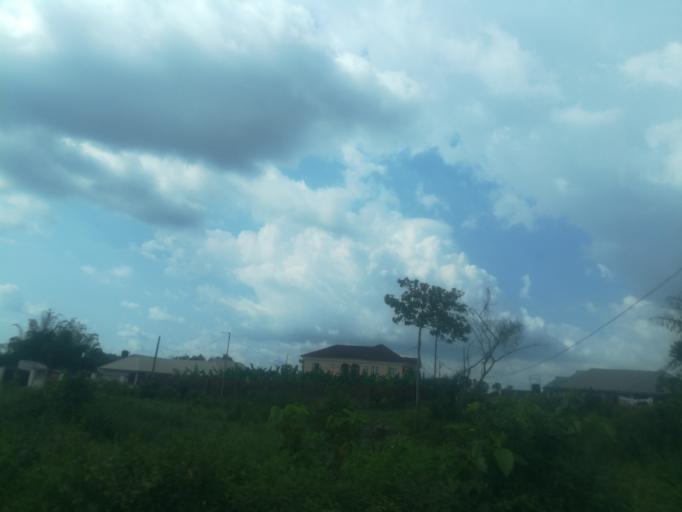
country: NG
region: Oyo
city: Ido
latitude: 7.4122
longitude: 3.8175
